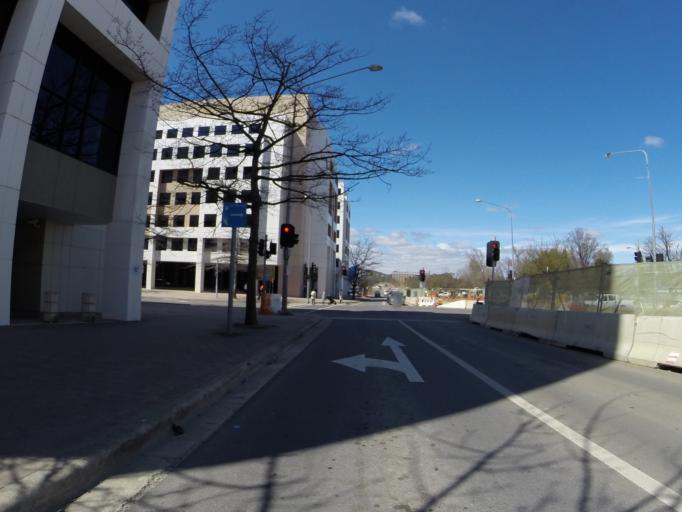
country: AU
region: Australian Capital Territory
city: Canberra
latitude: -35.2838
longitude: 149.1321
